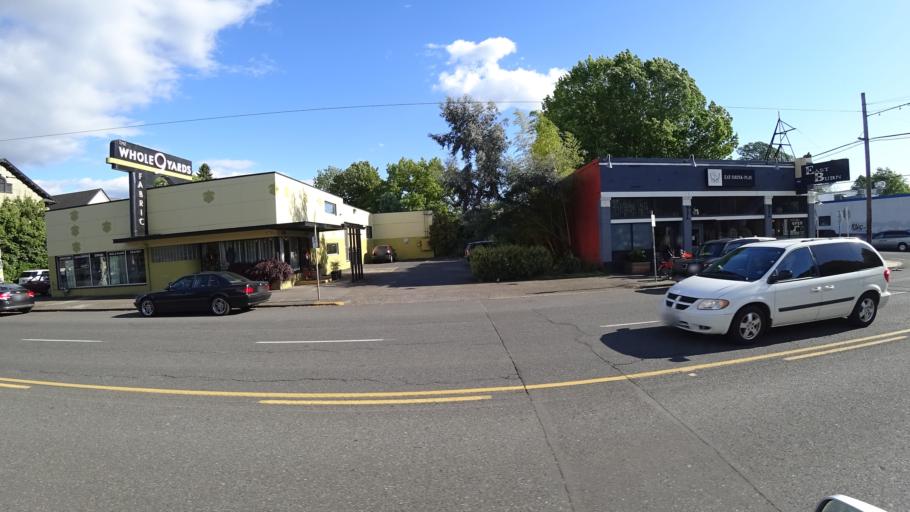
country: US
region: Oregon
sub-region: Multnomah County
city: Portland
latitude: 45.5229
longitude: -122.6475
